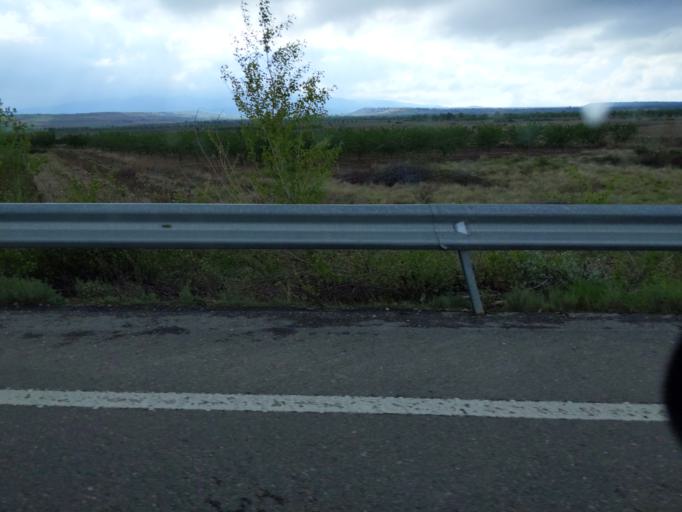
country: ES
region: La Rioja
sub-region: Provincia de La Rioja
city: Tudelilla
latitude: 42.2829
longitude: -2.0958
